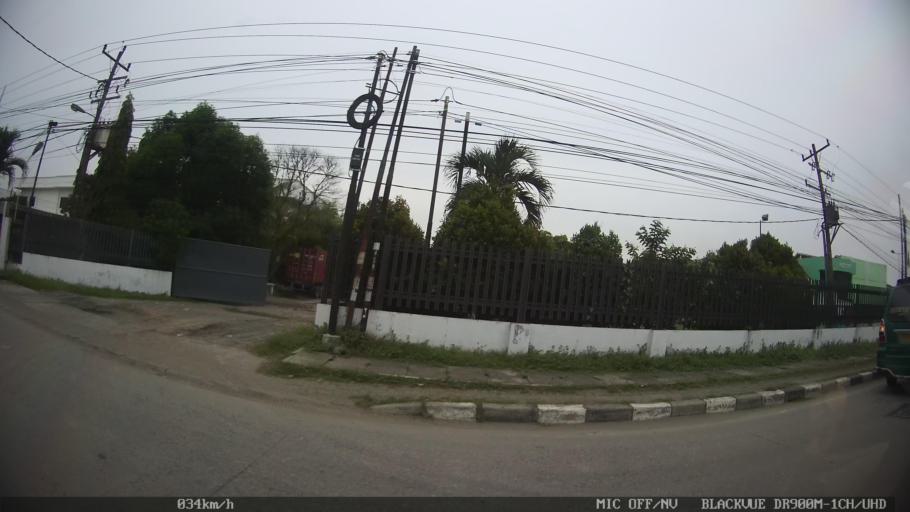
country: ID
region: North Sumatra
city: Deli Tua
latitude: 3.5324
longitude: 98.7294
